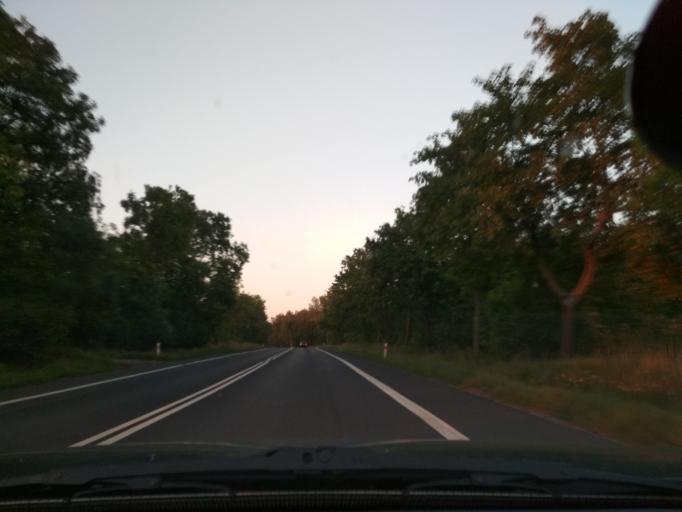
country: PL
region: Silesian Voivodeship
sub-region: Powiat bedzinski
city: Siewierz
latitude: 50.4810
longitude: 19.2700
